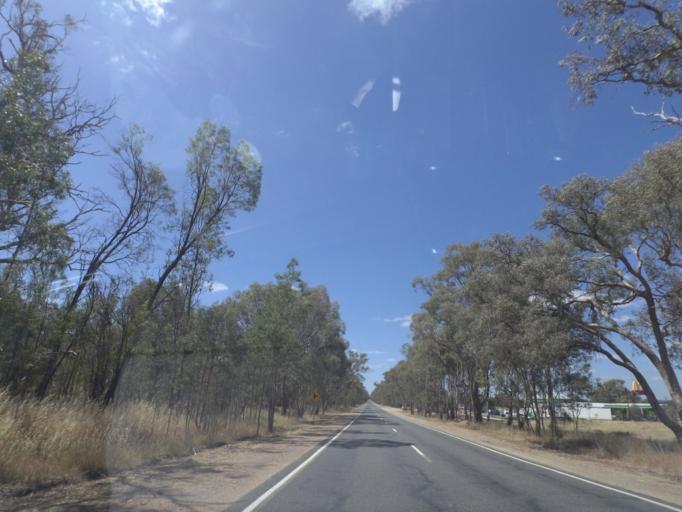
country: AU
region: Victoria
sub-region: Wangaratta
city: Wangaratta
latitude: -36.4397
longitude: 146.2466
